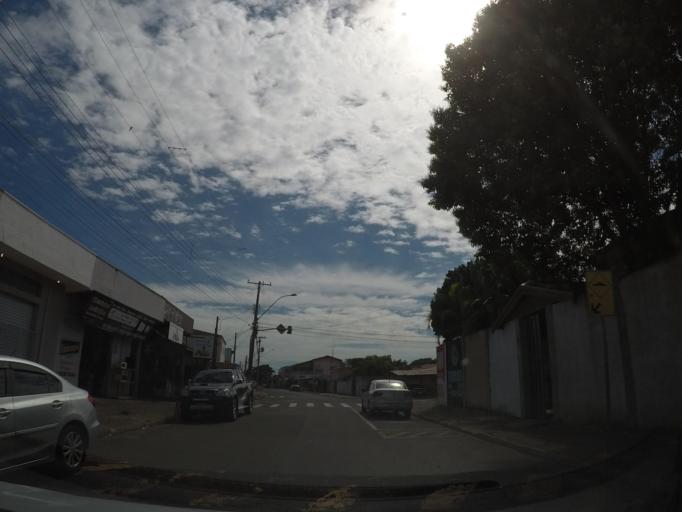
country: BR
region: Sao Paulo
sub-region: Hortolandia
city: Hortolandia
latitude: -22.8337
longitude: -47.1851
